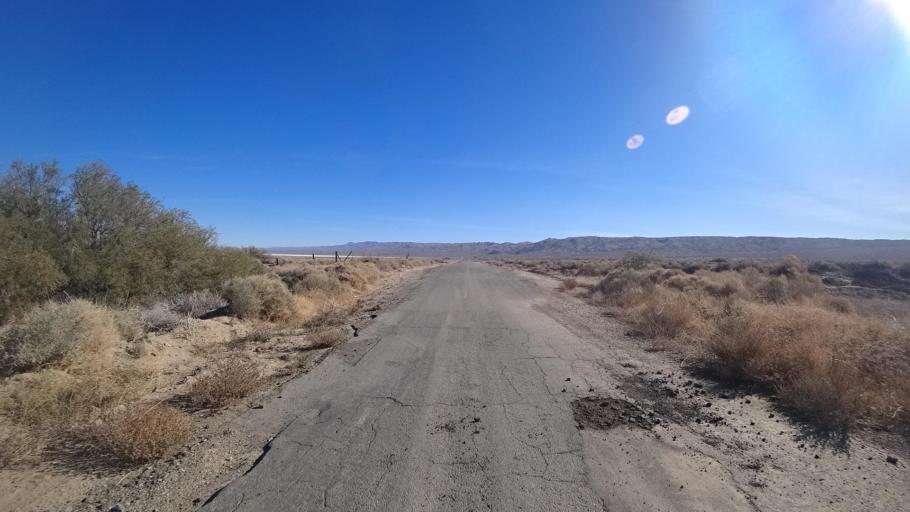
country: US
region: California
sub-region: Kern County
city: California City
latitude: 35.2870
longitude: -117.9228
